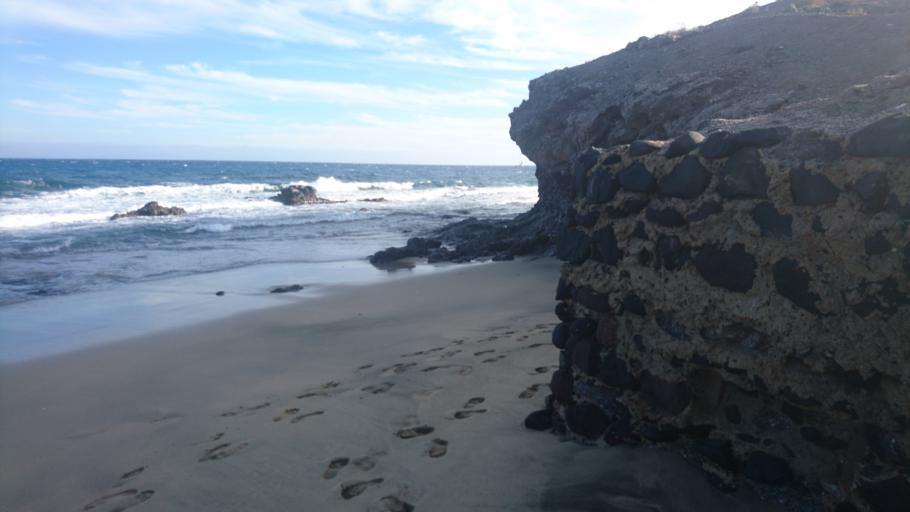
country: ES
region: Canary Islands
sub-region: Provincia de Las Palmas
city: Playa Blanca
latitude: 28.8404
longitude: -13.7854
